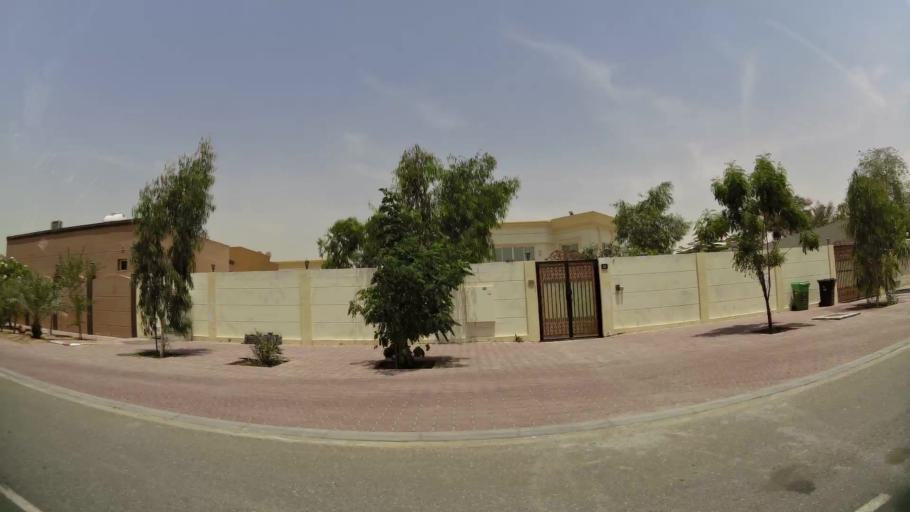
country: AE
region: Ash Shariqah
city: Sharjah
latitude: 25.1936
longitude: 55.3775
